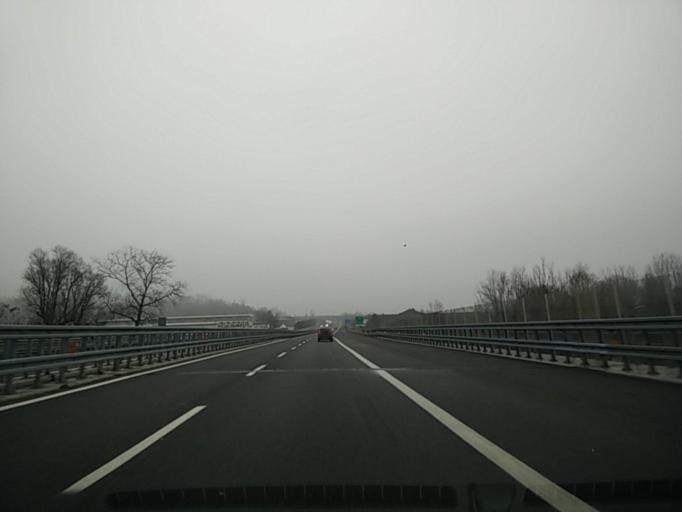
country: IT
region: Piedmont
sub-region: Provincia di Asti
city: Asti
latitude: 44.9130
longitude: 8.2313
